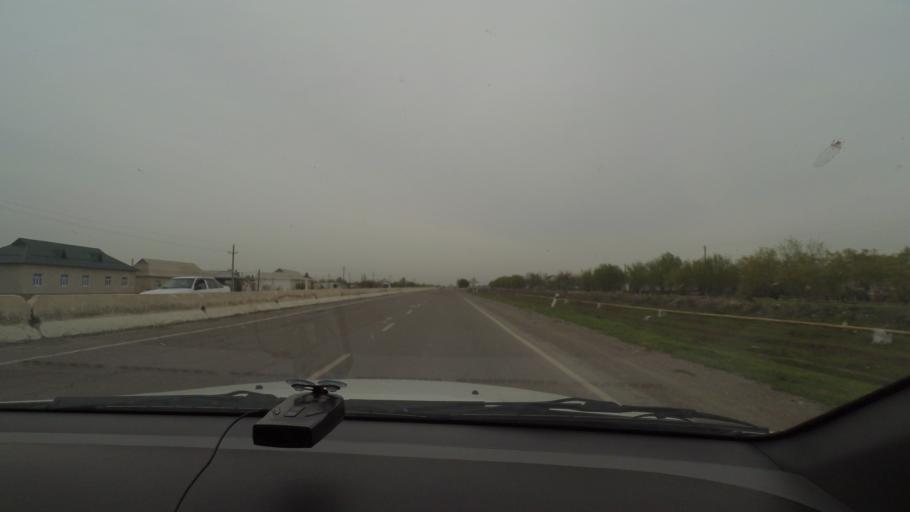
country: UZ
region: Sirdaryo
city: Guliston
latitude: 40.4922
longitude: 68.6890
